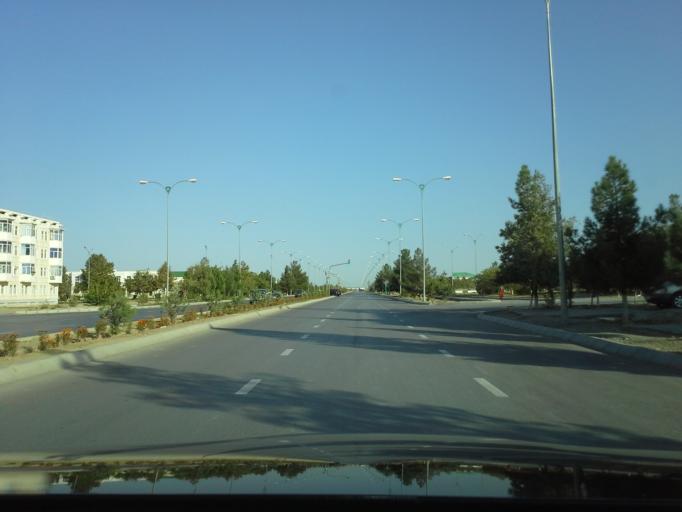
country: TM
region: Ahal
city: Abadan
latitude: 38.0540
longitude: 58.1551
